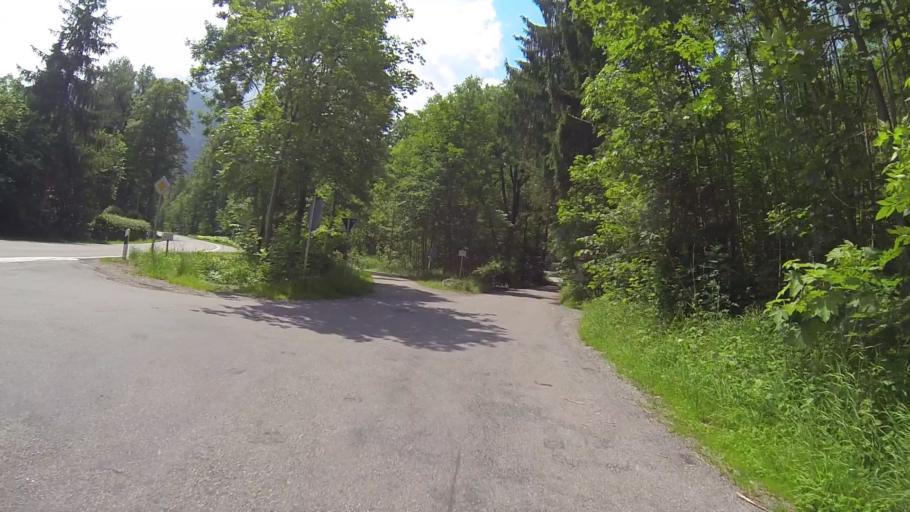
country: DE
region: Bavaria
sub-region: Swabia
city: Schwangau
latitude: 47.5639
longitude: 10.7272
